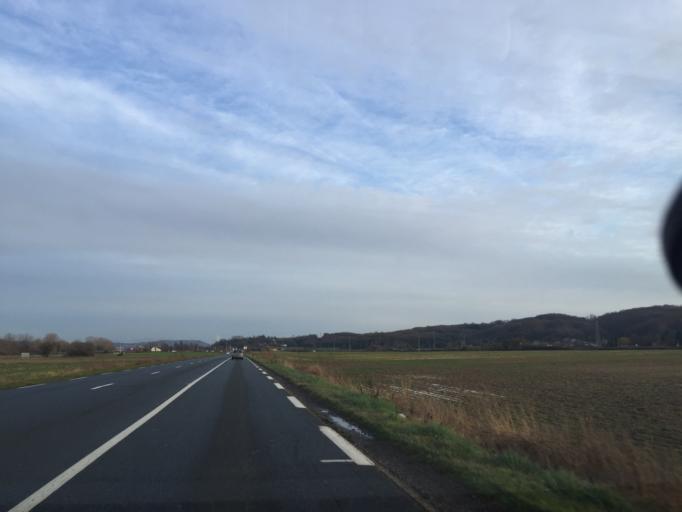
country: FR
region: Rhone-Alpes
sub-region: Departement de l'Isere
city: Vaulx-Milieu
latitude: 45.6169
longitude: 5.1882
